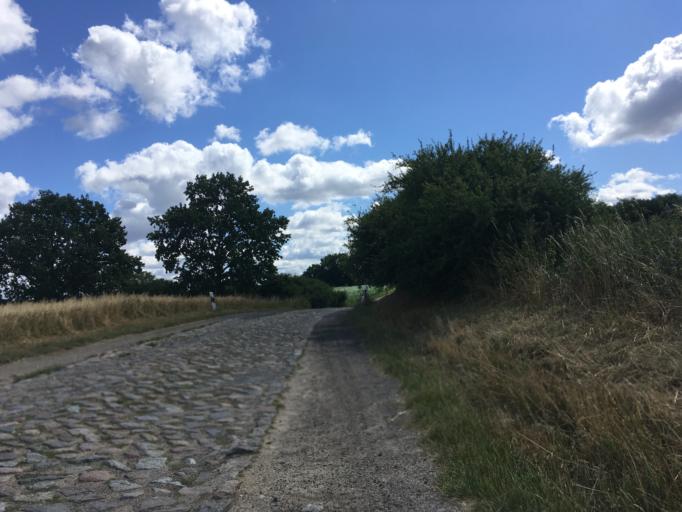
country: DE
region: Brandenburg
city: Mittenwalde
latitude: 53.1920
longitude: 13.6309
